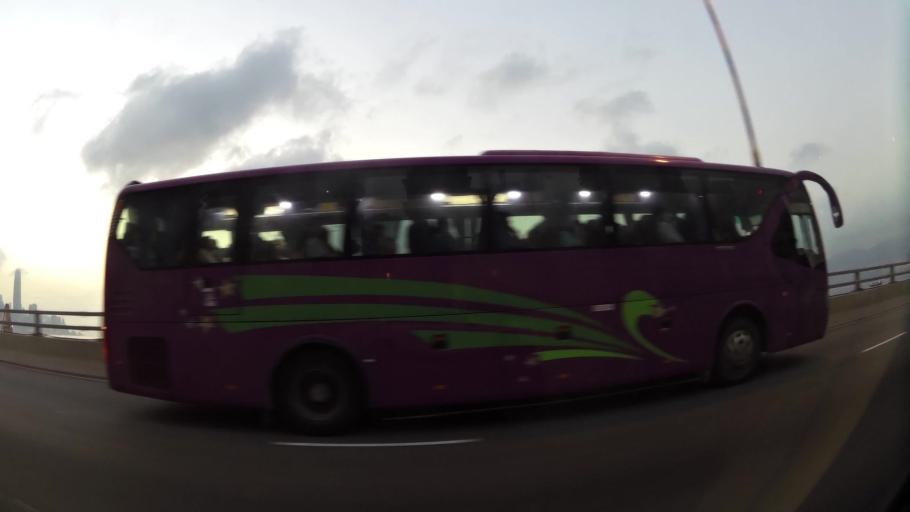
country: HK
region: Wanchai
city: Wan Chai
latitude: 22.2903
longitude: 114.1913
